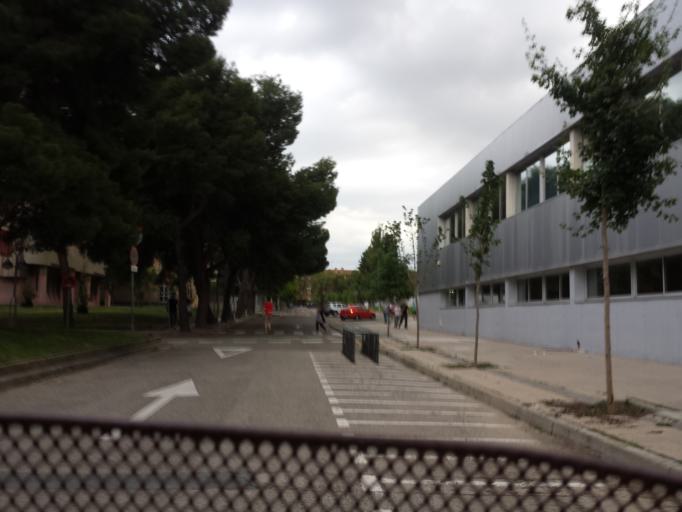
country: ES
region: Aragon
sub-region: Provincia de Zaragoza
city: Delicias
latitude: 41.6437
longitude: -0.8994
